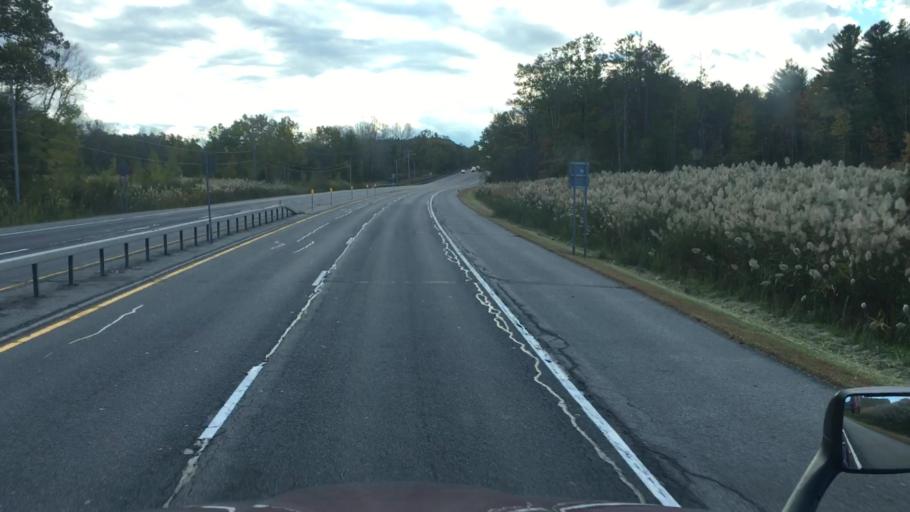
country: US
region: New York
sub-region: Saratoga County
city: Milton
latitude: 43.0472
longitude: -73.8140
